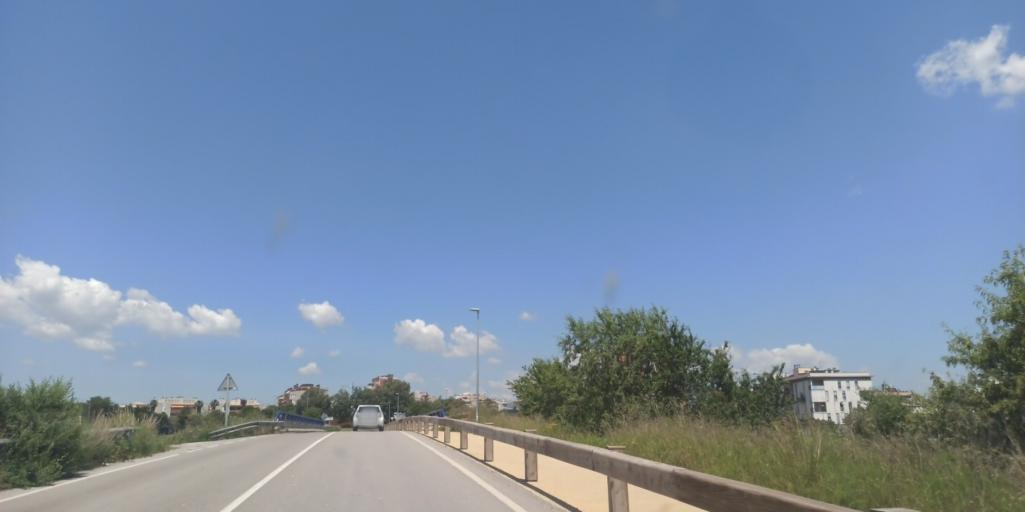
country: ES
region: Catalonia
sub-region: Provincia de Barcelona
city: Vilafranca del Penedes
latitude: 41.3333
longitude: 1.6978
